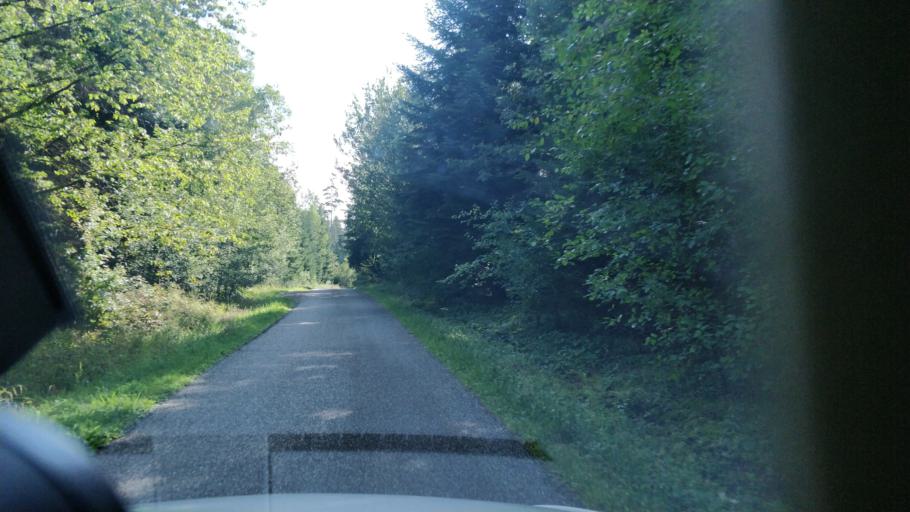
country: DE
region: Baden-Wuerttemberg
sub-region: Regierungsbezirk Stuttgart
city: Oberrot
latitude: 48.9936
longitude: 9.6598
